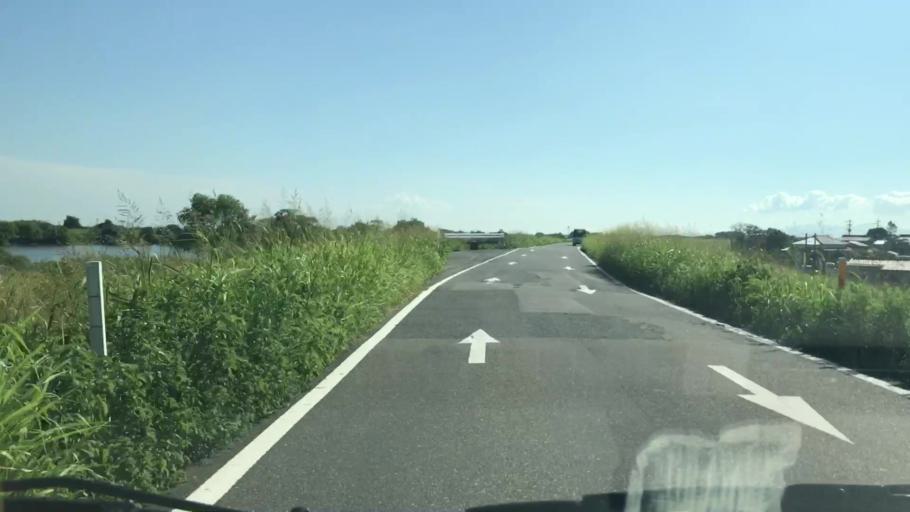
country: JP
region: Fukuoka
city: Kurume
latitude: 33.2804
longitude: 130.4478
